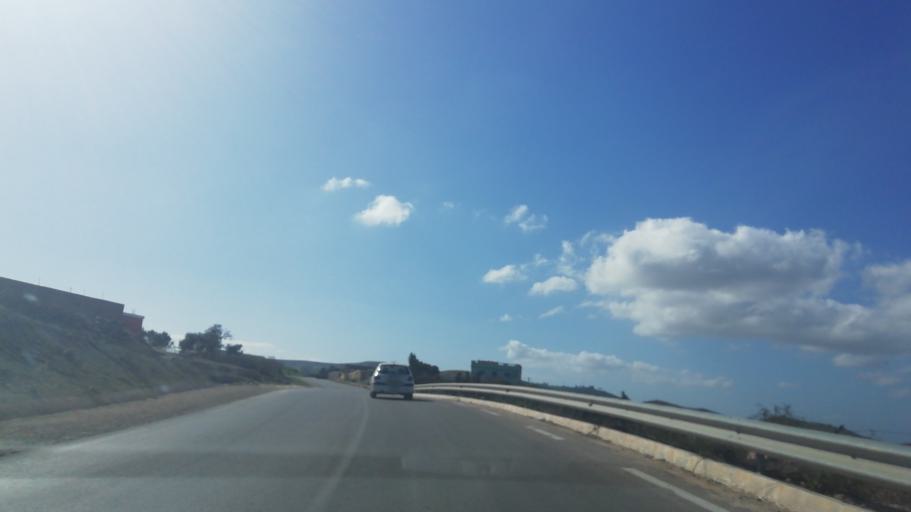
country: DZ
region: Relizane
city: Relizane
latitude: 36.0856
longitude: 0.5044
